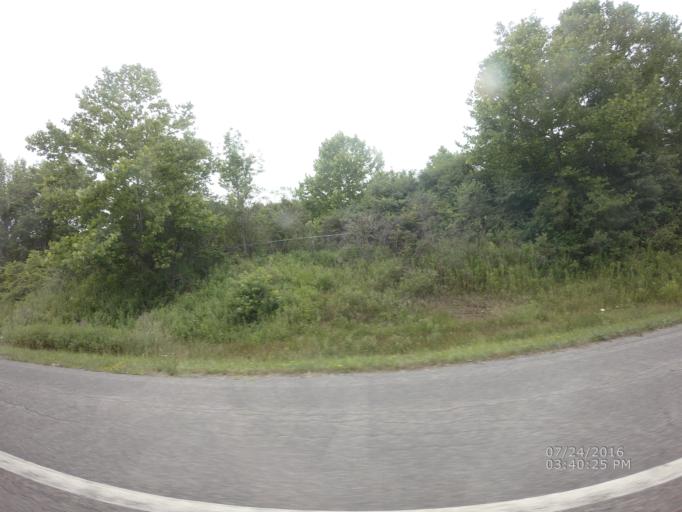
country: US
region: New York
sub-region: Onondaga County
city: Camillus
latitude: 43.0441
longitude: -76.3064
